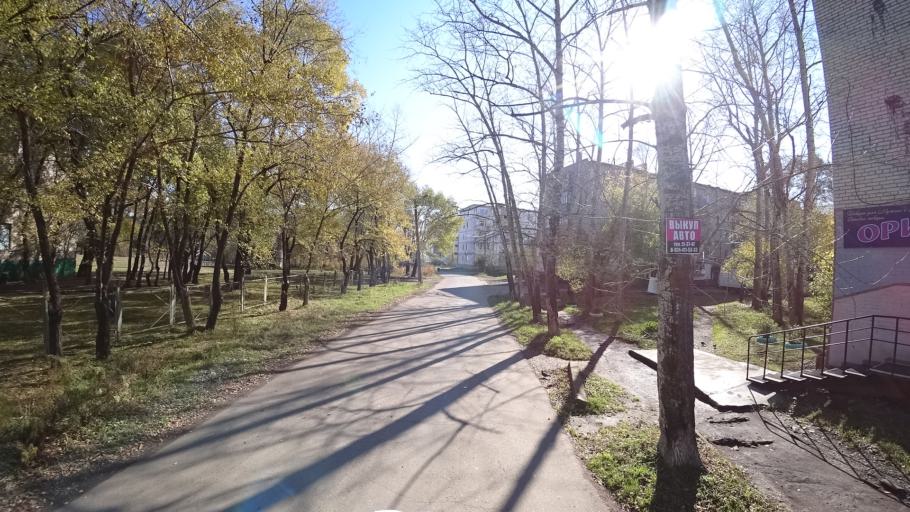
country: RU
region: Khabarovsk Krai
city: Amursk
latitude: 50.0979
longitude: 136.5140
